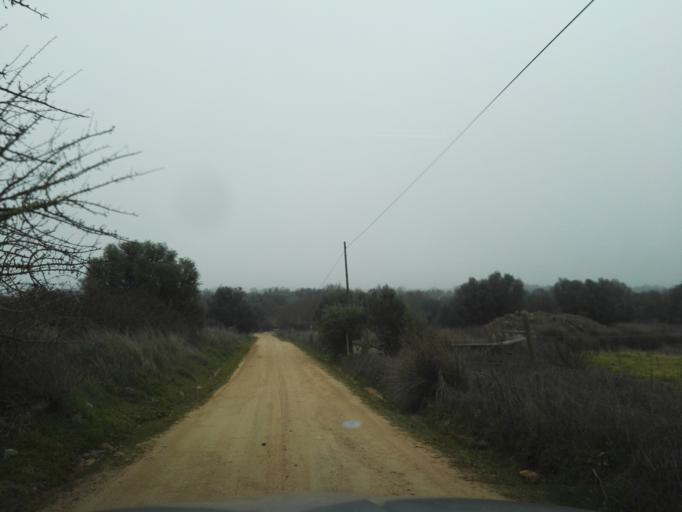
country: PT
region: Evora
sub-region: Montemor-O-Novo
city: Montemor-o-Novo
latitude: 38.7729
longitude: -8.2300
